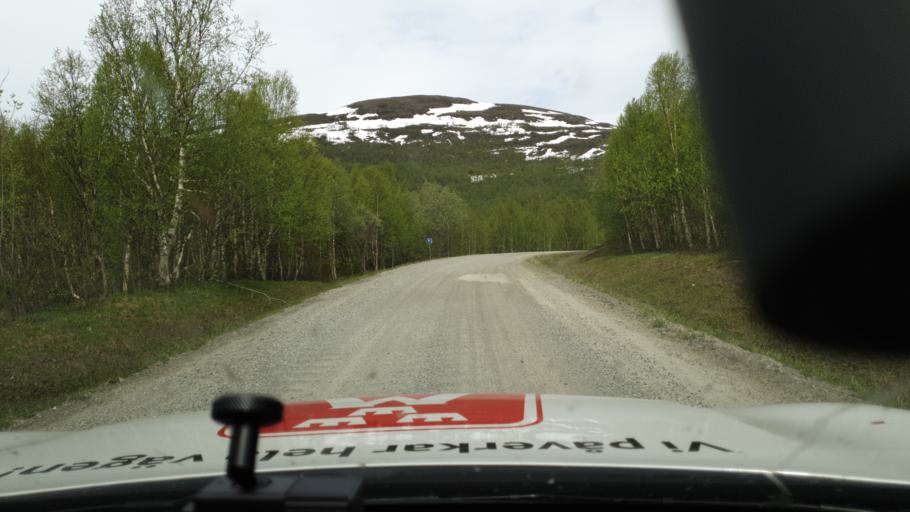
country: NO
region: Nordland
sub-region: Rana
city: Mo i Rana
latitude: 65.7522
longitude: 15.1901
